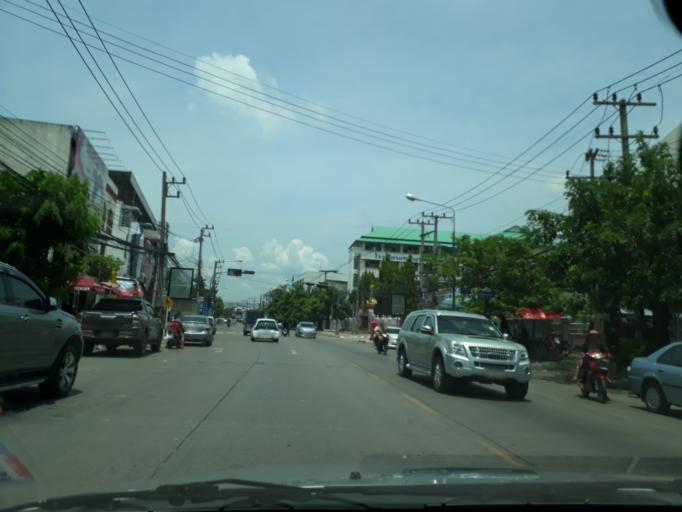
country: TH
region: Khon Kaen
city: Khon Kaen
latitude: 16.4135
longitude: 102.8307
